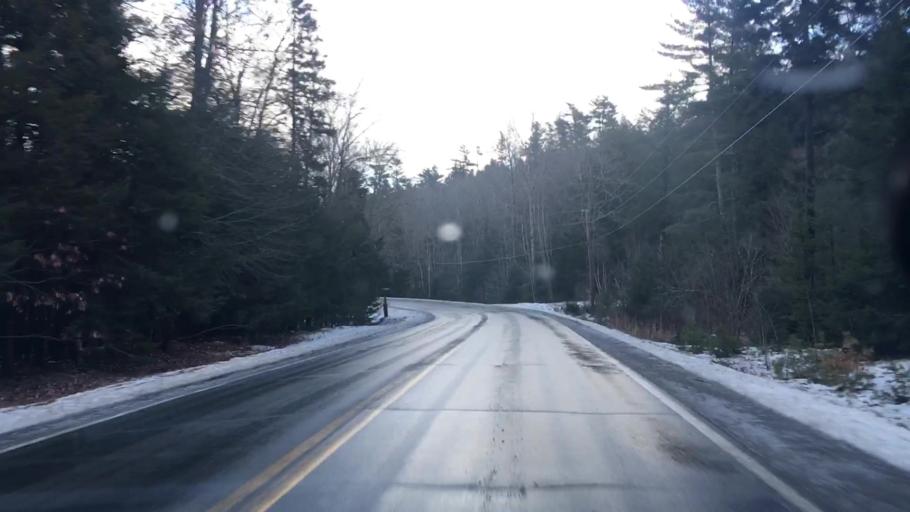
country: US
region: Maine
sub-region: Hancock County
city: Dedham
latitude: 44.6436
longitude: -68.6935
